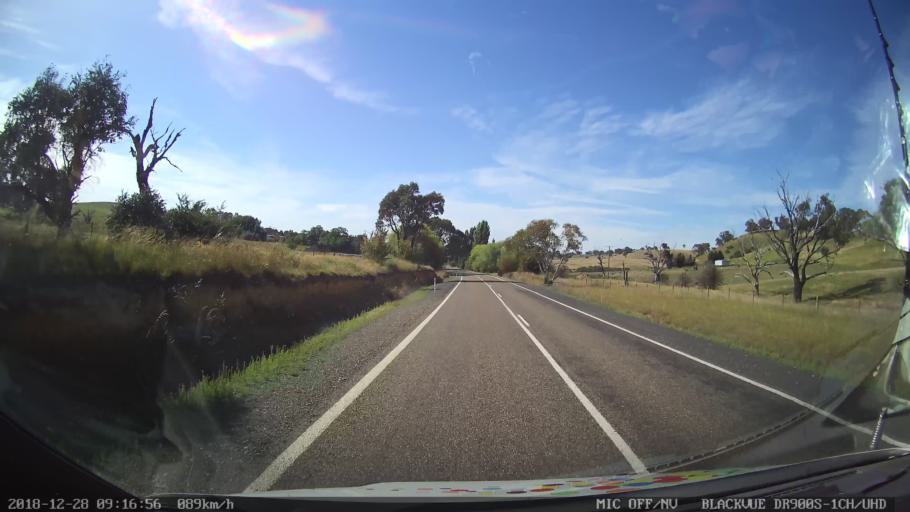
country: AU
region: New South Wales
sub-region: Upper Lachlan Shire
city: Crookwell
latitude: -34.3150
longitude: 149.3578
